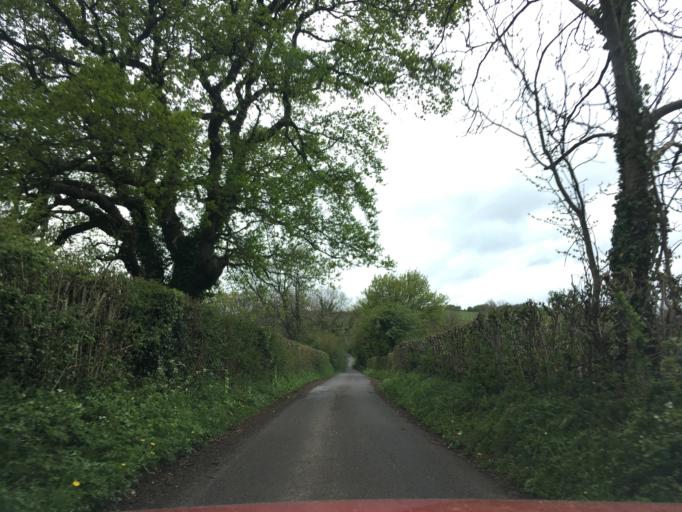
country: GB
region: England
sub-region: Bath and North East Somerset
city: Clutton
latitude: 51.3375
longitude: -2.5366
